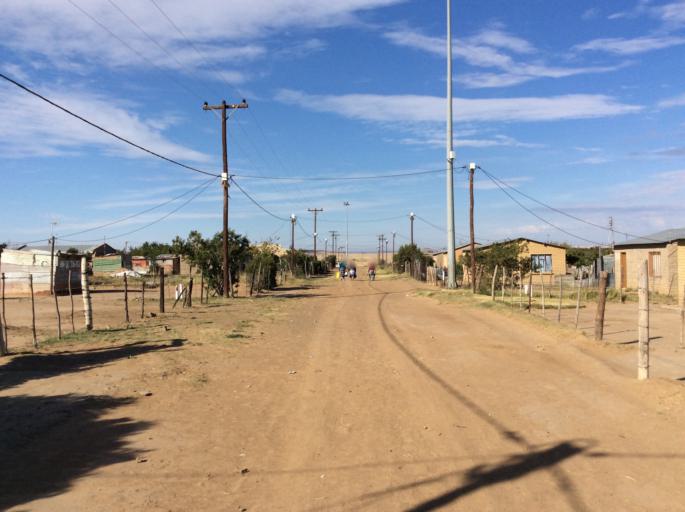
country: LS
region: Mafeteng
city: Mafeteng
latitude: -29.7119
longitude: 27.0152
